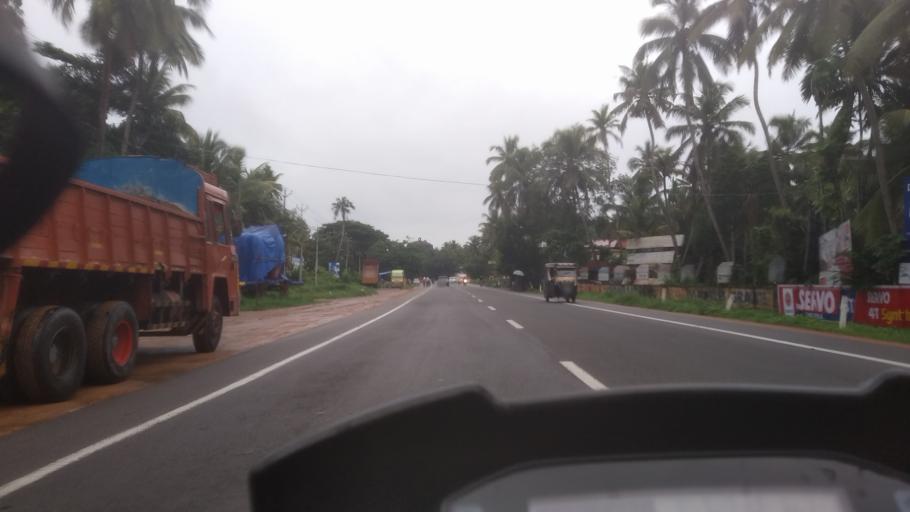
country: IN
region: Kerala
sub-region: Alappuzha
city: Kayankulam
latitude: 9.1581
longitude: 76.5088
